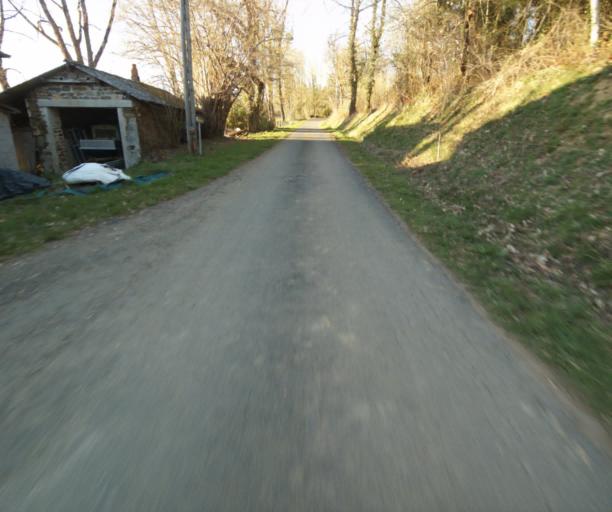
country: FR
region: Limousin
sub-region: Departement de la Correze
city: Saint-Clement
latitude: 45.3380
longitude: 1.7134
